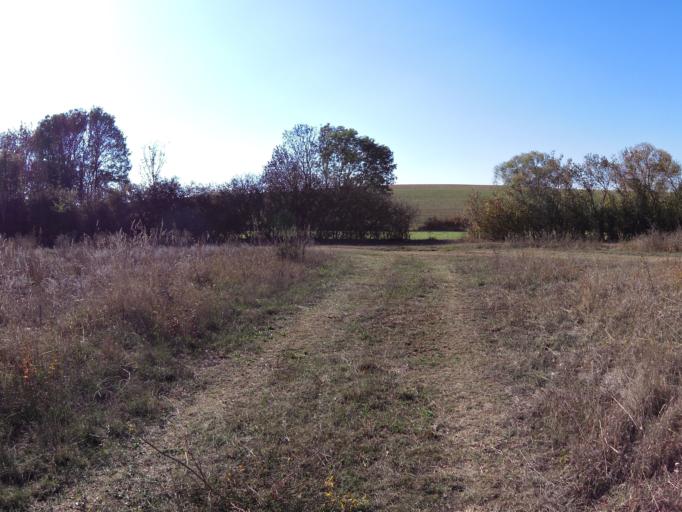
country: DE
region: Bavaria
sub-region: Regierungsbezirk Unterfranken
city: Eibelstadt
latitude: 49.7124
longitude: 9.9845
